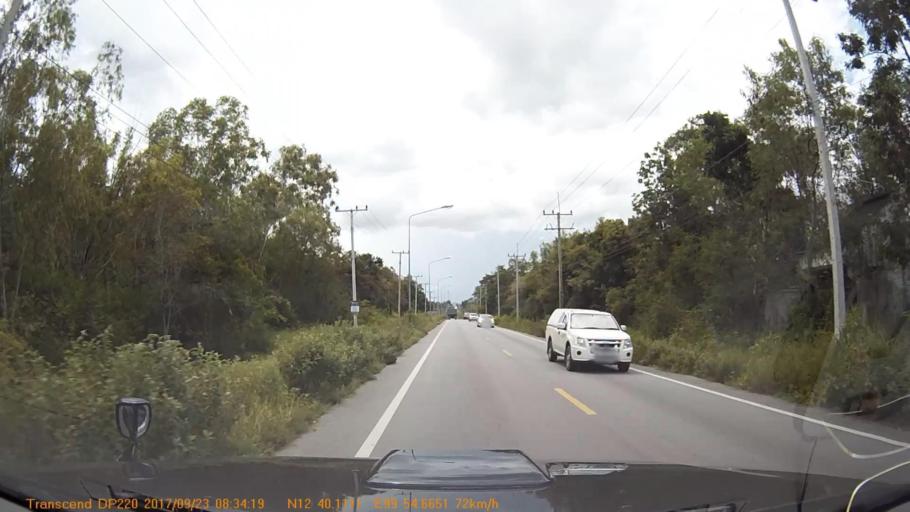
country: TH
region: Prachuap Khiri Khan
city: Hua Hin
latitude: 12.6685
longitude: 99.9107
